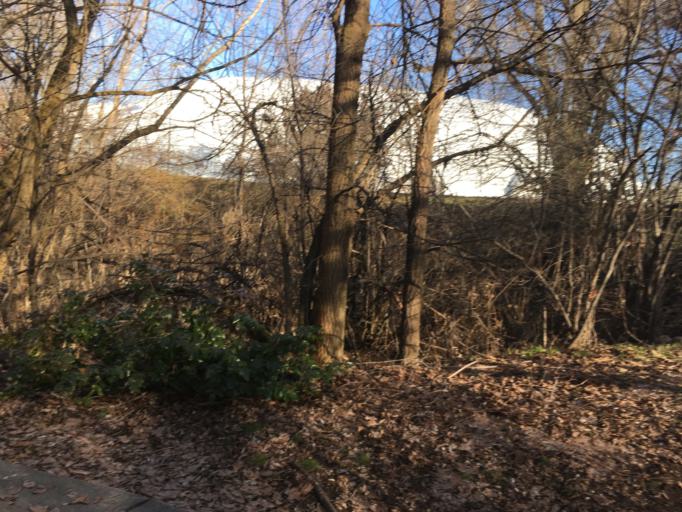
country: US
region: Utah
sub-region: Davis County
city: Layton
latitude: 41.0679
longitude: -111.9630
